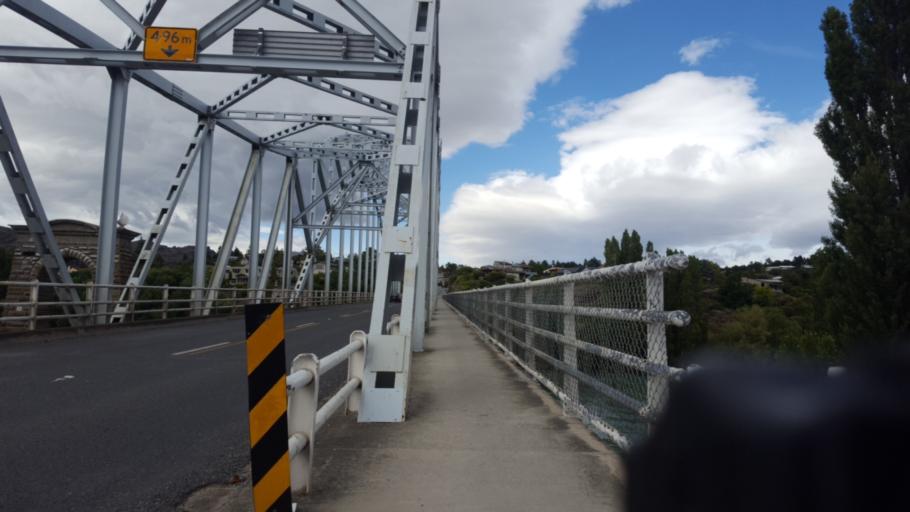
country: NZ
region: Otago
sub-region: Queenstown-Lakes District
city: Wanaka
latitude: -45.2578
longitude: 169.3911
